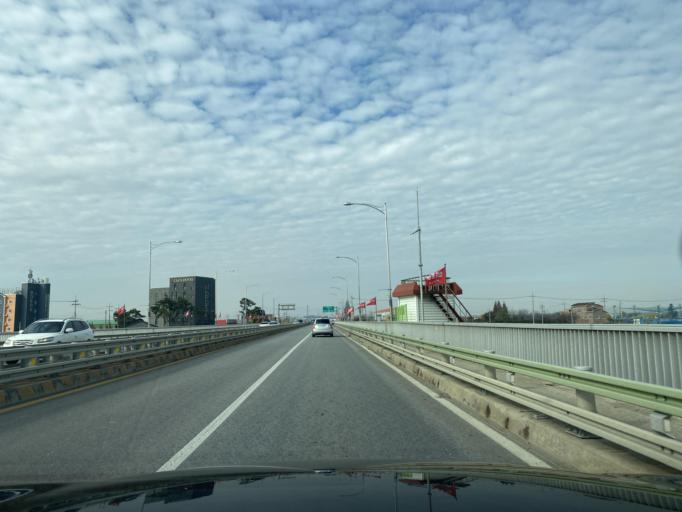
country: KR
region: Chungcheongnam-do
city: Yesan
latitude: 36.6841
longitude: 126.8213
